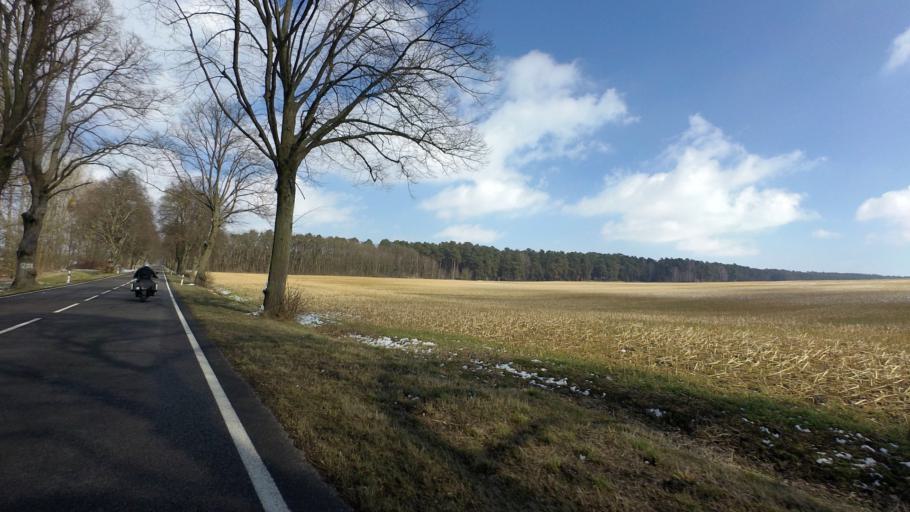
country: DE
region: Brandenburg
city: Werftpfuhl
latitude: 52.7055
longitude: 13.8369
